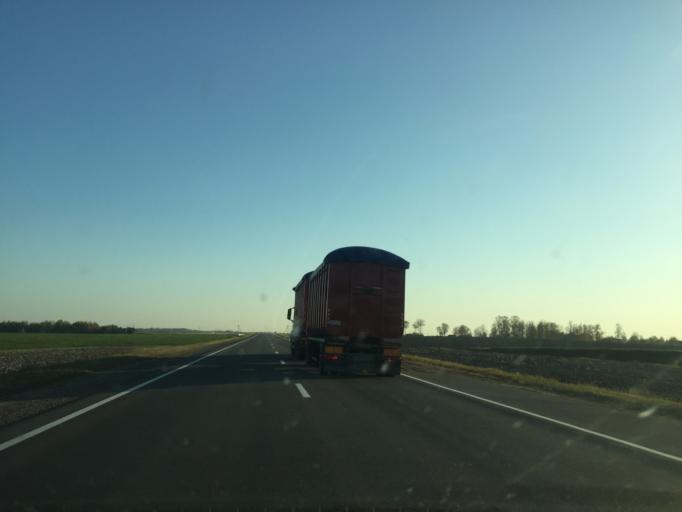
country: BY
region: Mogilev
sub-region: Mahilyowski Rayon
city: Kadino
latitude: 53.8506
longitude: 30.4801
